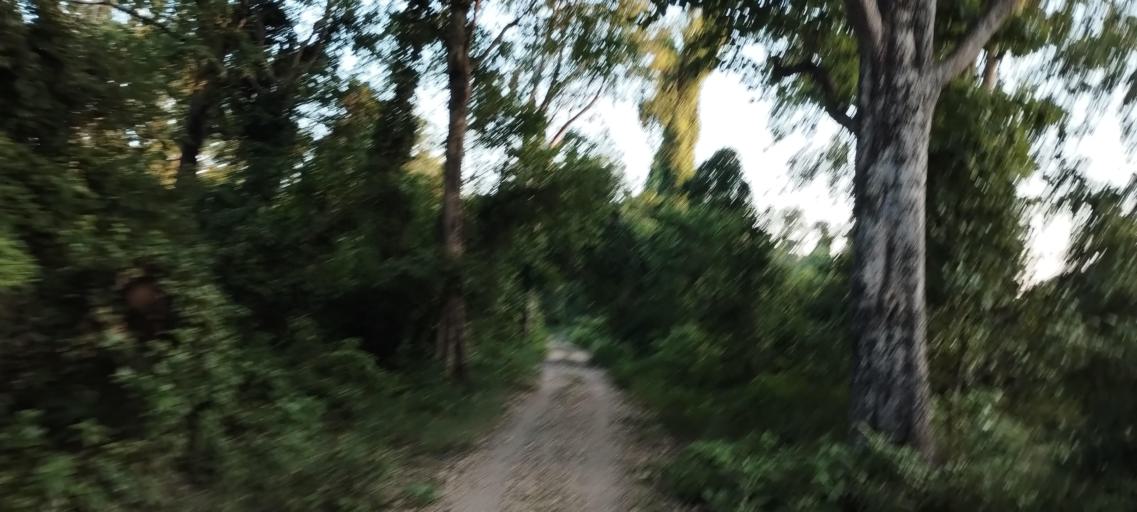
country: NP
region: Far Western
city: Tikapur
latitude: 28.4571
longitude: 81.2424
